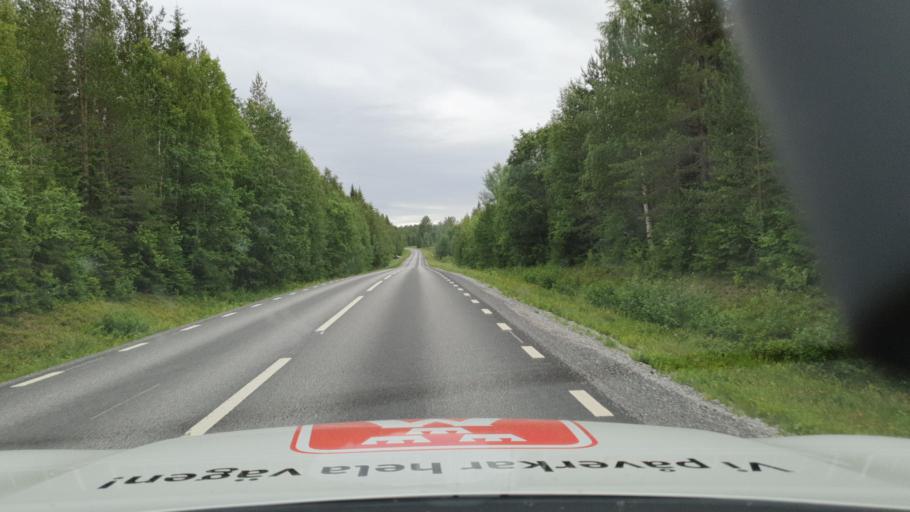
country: SE
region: Vaesterbotten
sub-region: Nordmalings Kommun
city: Nordmaling
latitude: 63.7218
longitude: 19.6435
